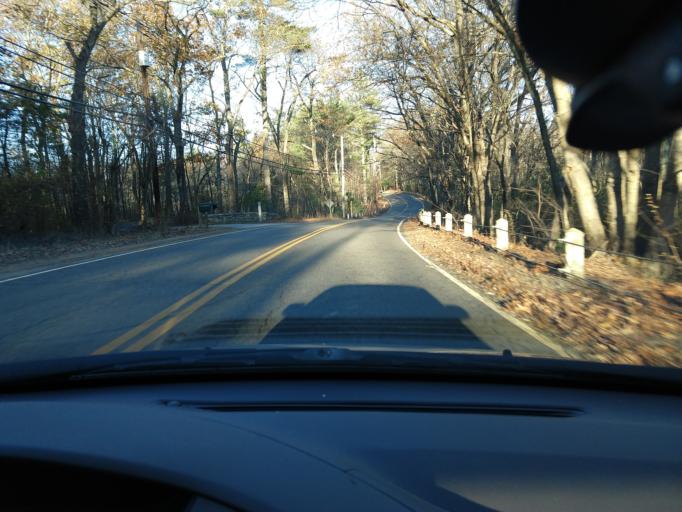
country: US
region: Massachusetts
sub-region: Middlesex County
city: Carlisle
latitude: 42.5207
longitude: -71.3622
